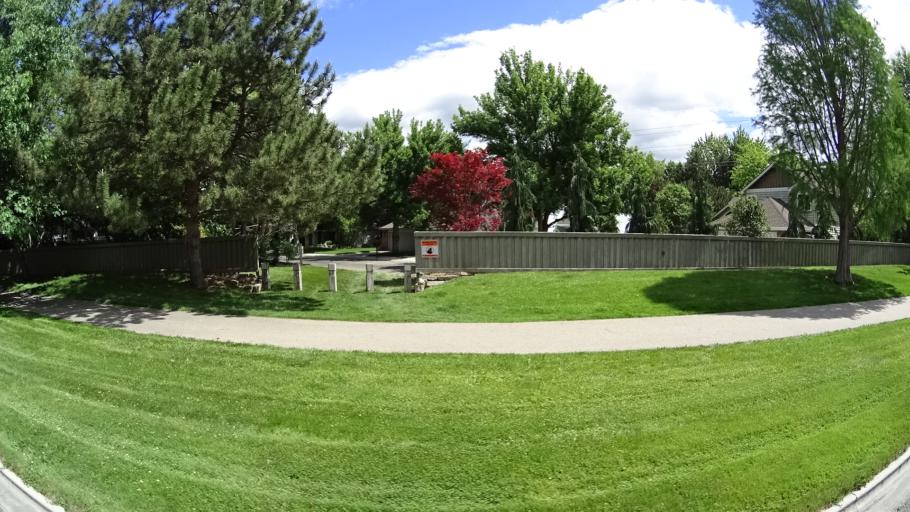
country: US
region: Idaho
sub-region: Ada County
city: Boise
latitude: 43.5790
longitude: -116.1594
